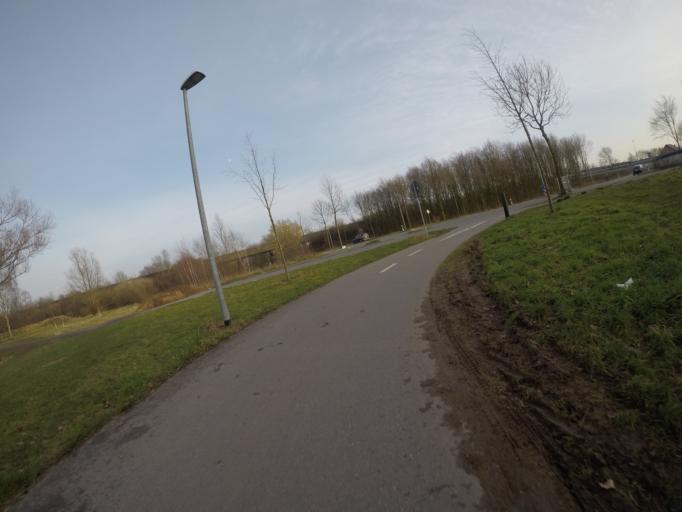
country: DE
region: North Rhine-Westphalia
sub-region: Regierungsbezirk Dusseldorf
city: Bocholt
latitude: 51.8266
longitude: 6.5964
